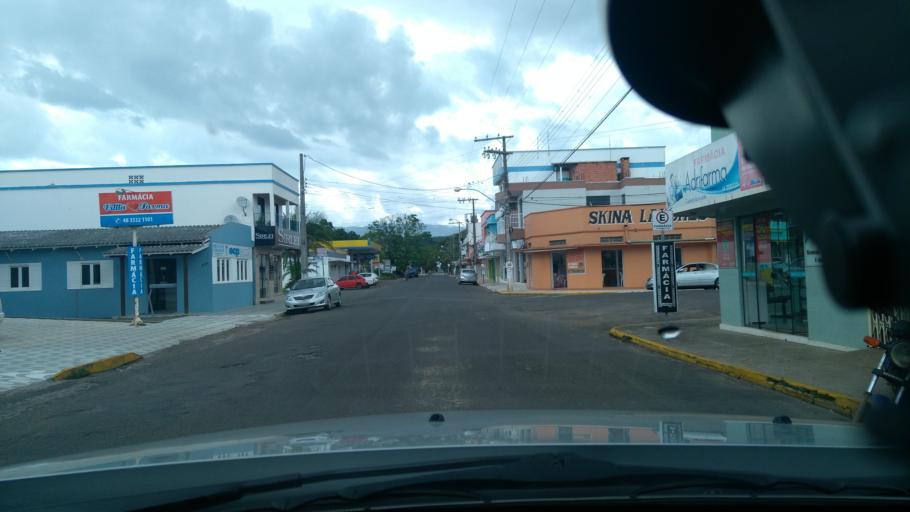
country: BR
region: Rio Grande do Sul
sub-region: Torres
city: Torres
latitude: -29.1966
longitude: -49.9488
